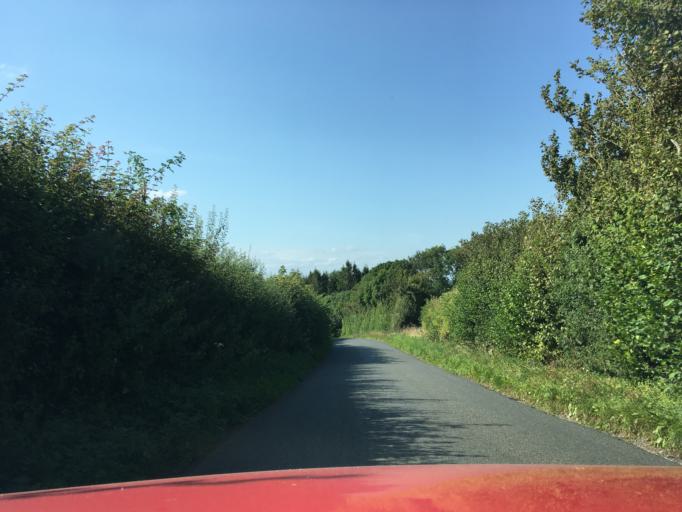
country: GB
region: England
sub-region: Gloucestershire
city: Dursley
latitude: 51.6721
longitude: -2.2931
